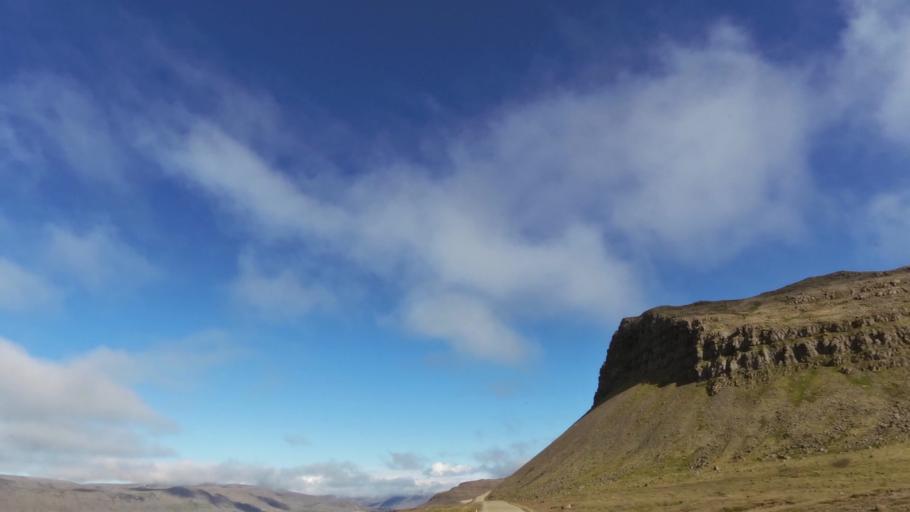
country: IS
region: West
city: Olafsvik
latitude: 65.5696
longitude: -24.0571
